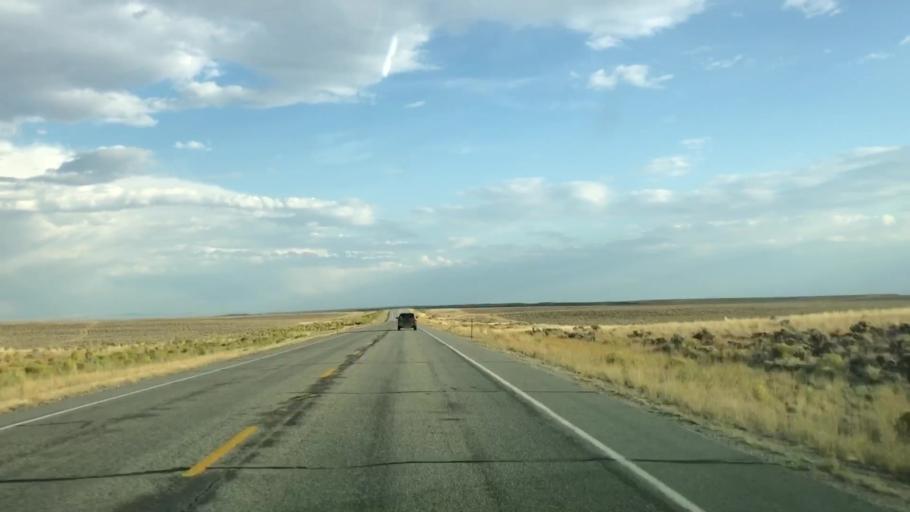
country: US
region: Wyoming
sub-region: Sublette County
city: Marbleton
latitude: 42.3253
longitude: -109.5120
